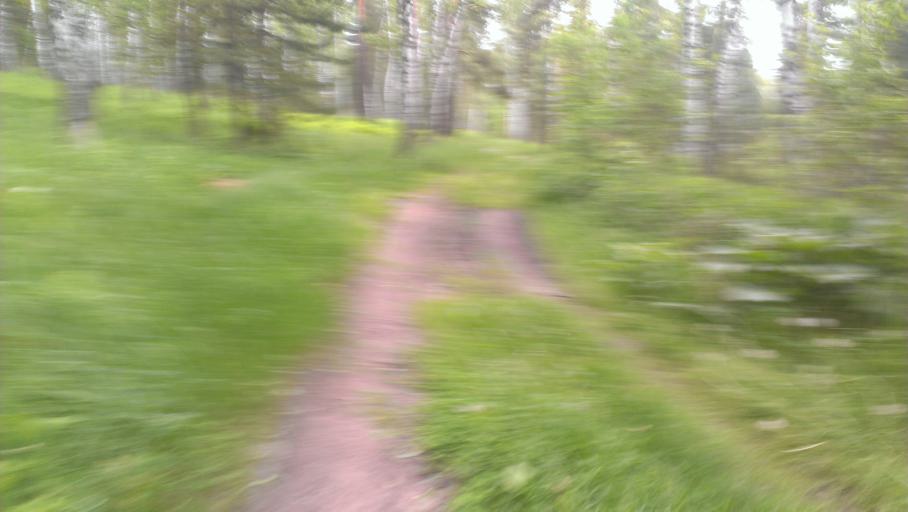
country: RU
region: Altai Krai
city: Sannikovo
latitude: 53.3400
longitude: 84.0486
